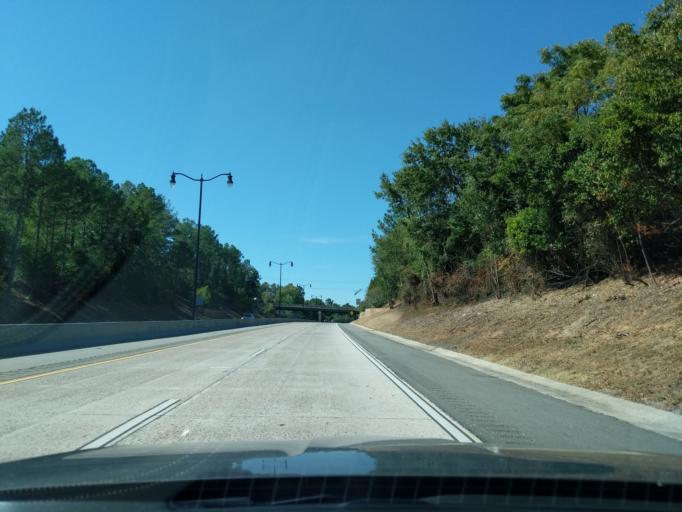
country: US
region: Georgia
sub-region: Richmond County
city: Augusta
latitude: 33.4862
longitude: -82.0043
